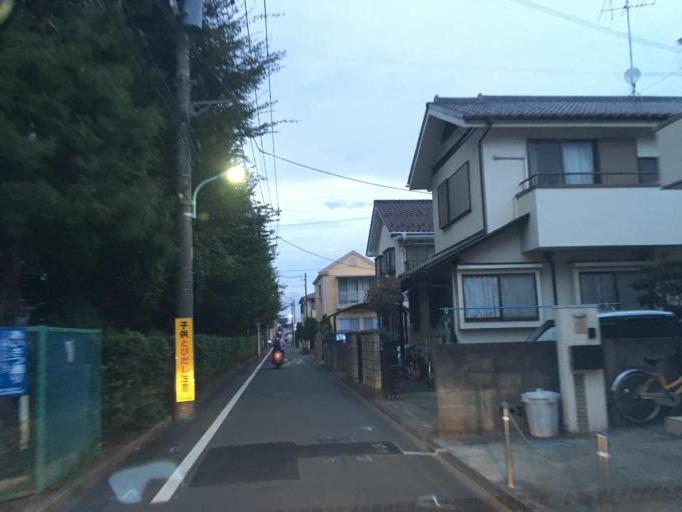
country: JP
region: Tokyo
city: Kokubunji
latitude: 35.7140
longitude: 139.4555
